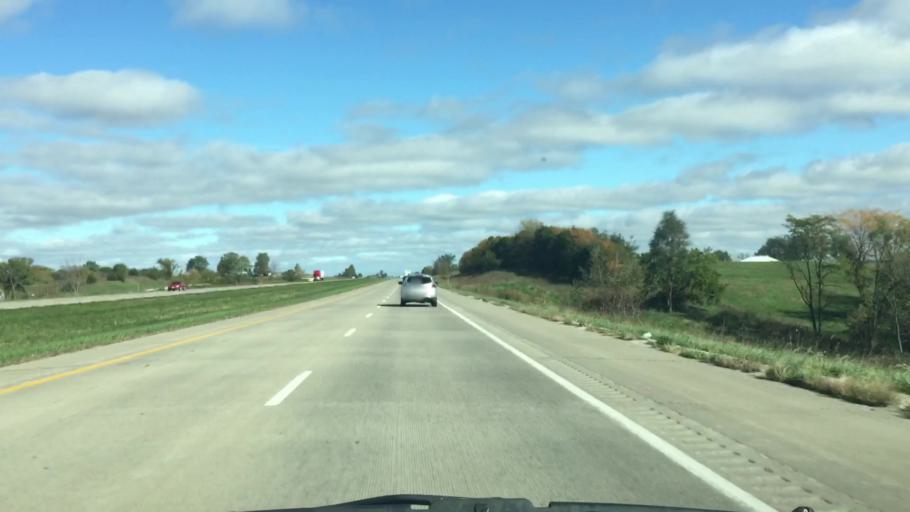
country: US
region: Iowa
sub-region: Decatur County
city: Leon
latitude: 40.7610
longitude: -93.8365
